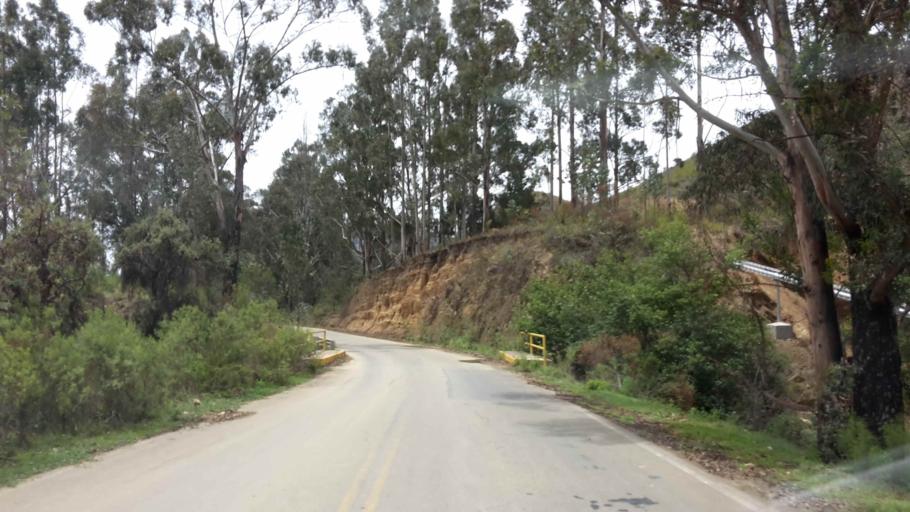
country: BO
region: Cochabamba
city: Totora
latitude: -17.6598
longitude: -65.2263
